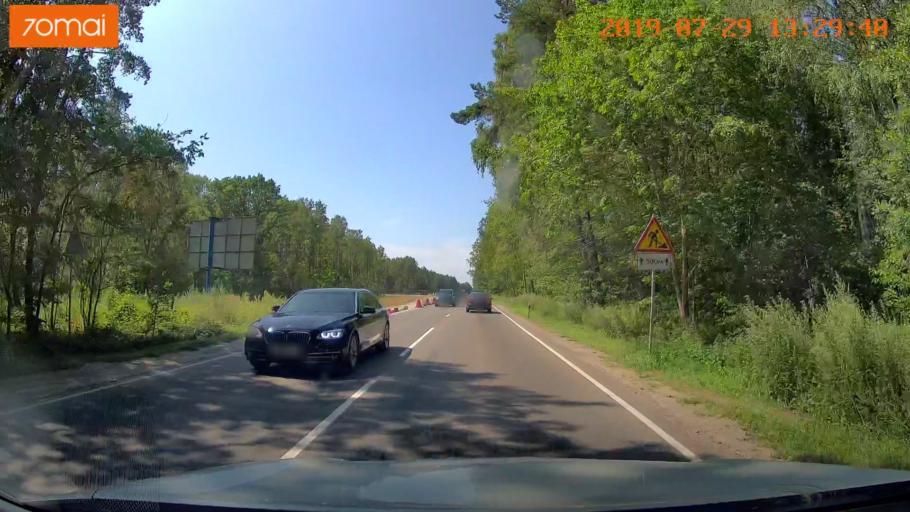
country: RU
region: Kaliningrad
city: Vzmorye
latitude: 54.7017
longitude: 20.2651
